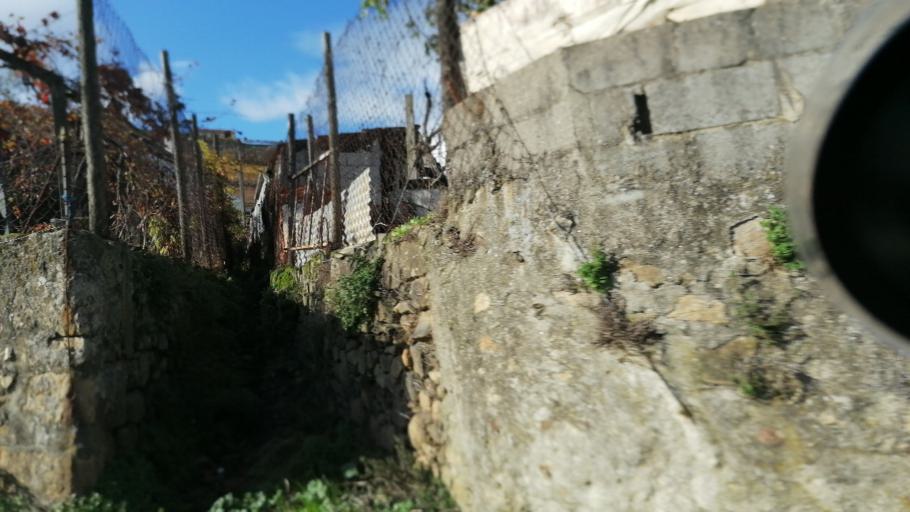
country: PT
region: Vila Real
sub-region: Peso da Regua
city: Peso da Regua
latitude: 41.1303
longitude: -7.7956
